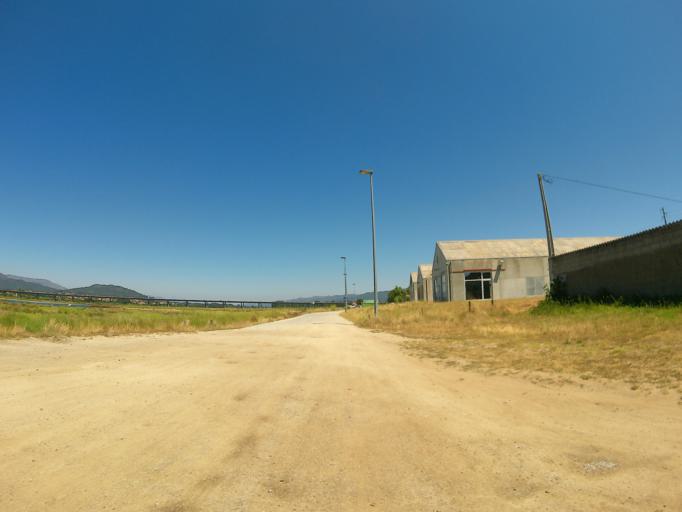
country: PT
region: Viana do Castelo
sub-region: Viana do Castelo
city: Meadela
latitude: 41.6881
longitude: -8.7948
